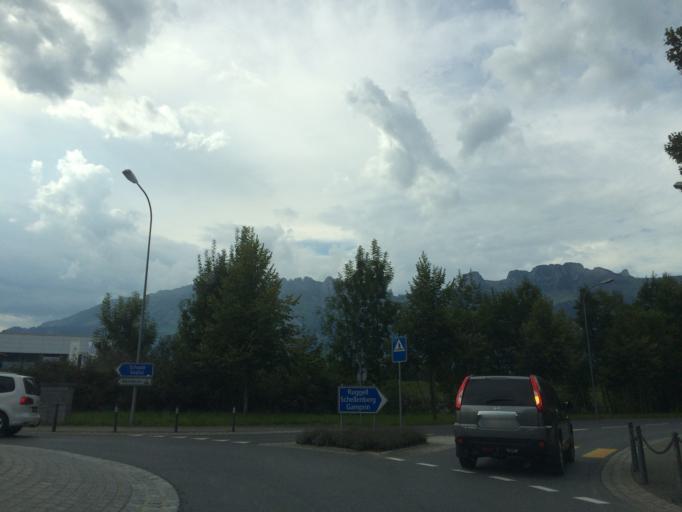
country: LI
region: Gamprin
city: Gamprin
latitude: 47.2110
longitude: 9.5025
